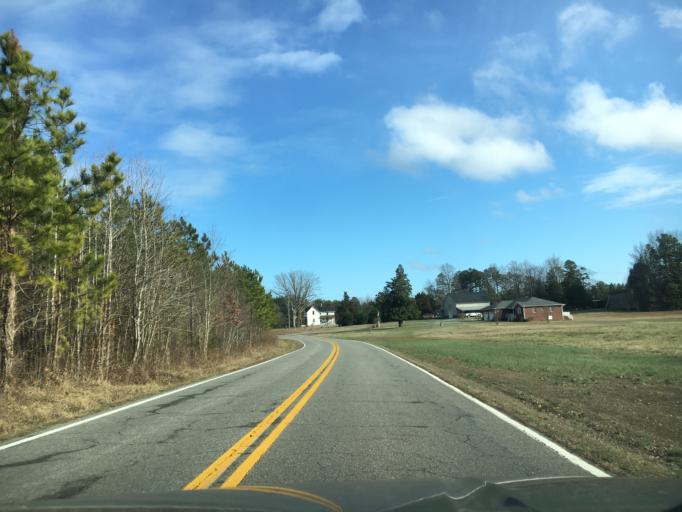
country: US
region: Virginia
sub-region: Halifax County
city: South Boston
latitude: 36.7329
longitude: -78.8698
